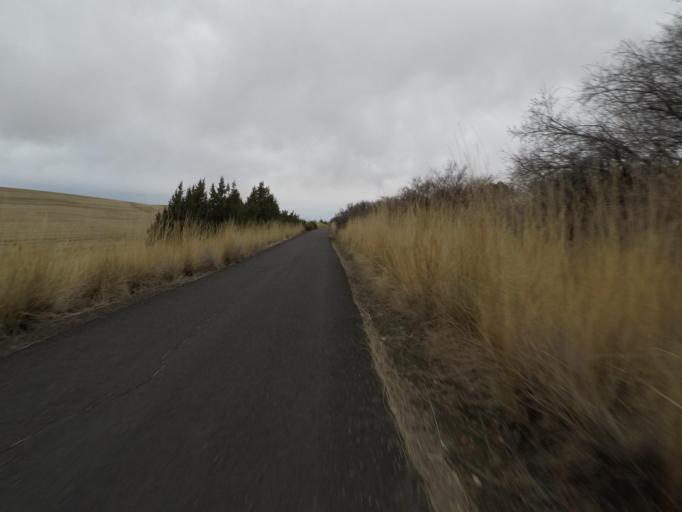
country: US
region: Washington
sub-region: Walla Walla County
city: Walla Walla East
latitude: 46.0646
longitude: -118.2678
